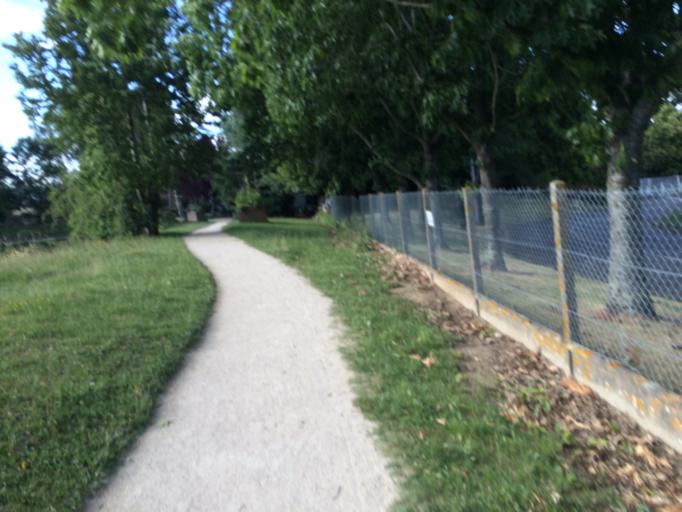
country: FR
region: Ile-de-France
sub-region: Departement de l'Essonne
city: Orsay
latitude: 48.6933
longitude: 2.2096
